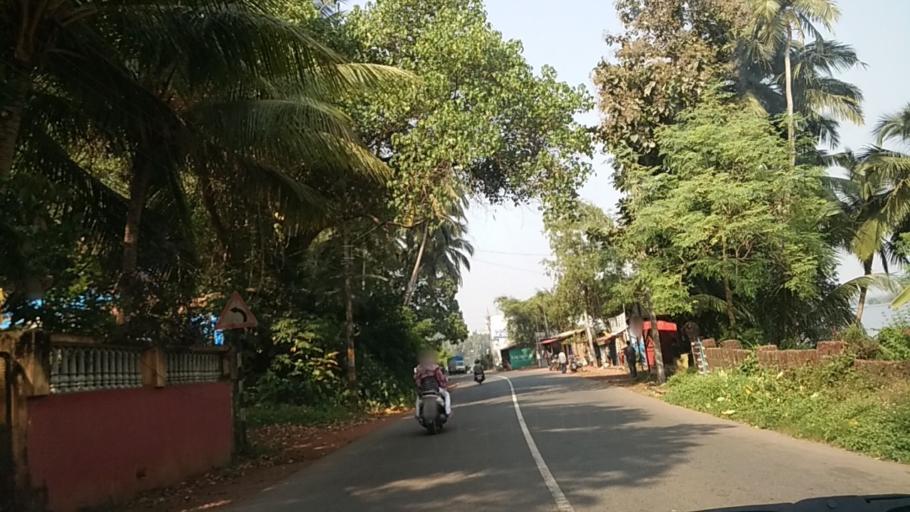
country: IN
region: Goa
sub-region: North Goa
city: Bambolim
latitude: 15.4997
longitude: 73.8831
